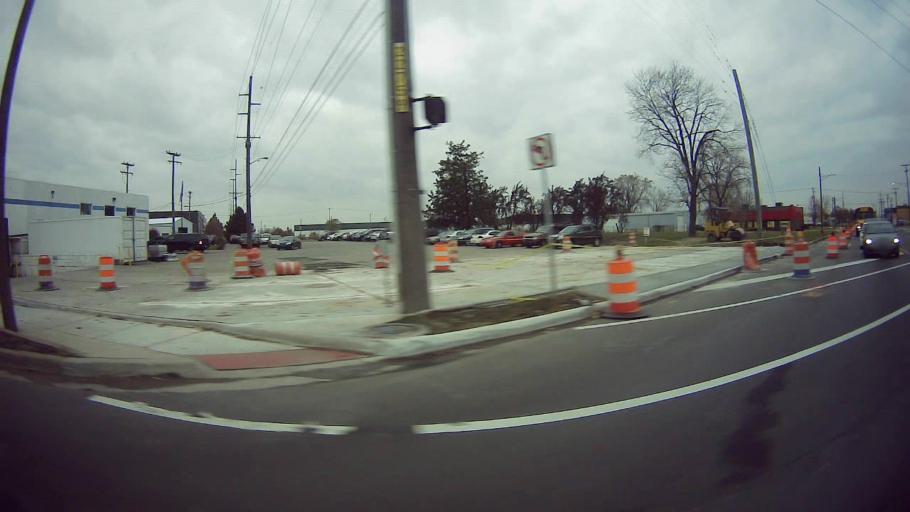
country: US
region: Michigan
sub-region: Macomb County
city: Eastpointe
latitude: 42.4711
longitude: -82.9864
